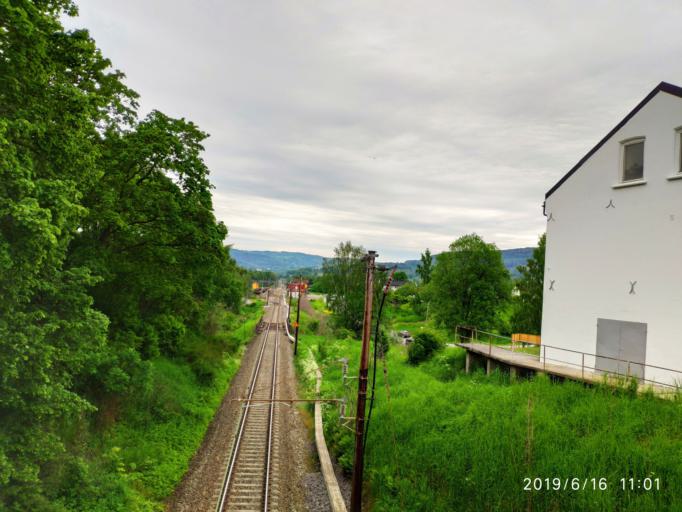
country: NO
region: Oppland
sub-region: Jevnaker
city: Jevnaker
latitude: 60.2378
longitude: 10.3998
